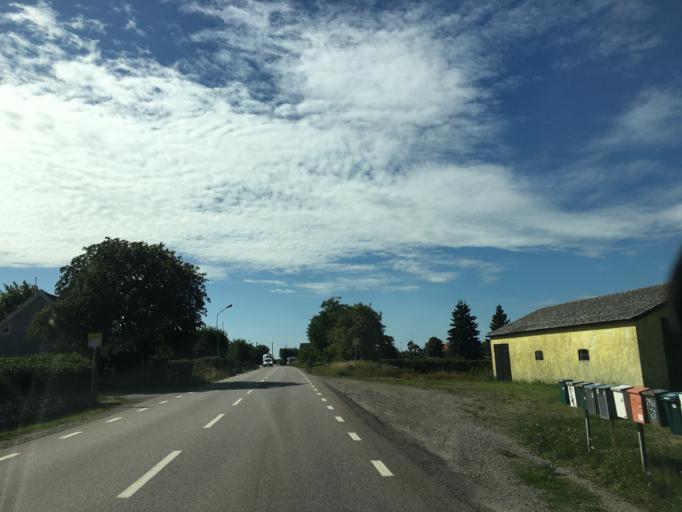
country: SE
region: Kalmar
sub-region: Morbylanga Kommun
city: Moerbylanga
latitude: 56.5090
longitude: 16.4368
